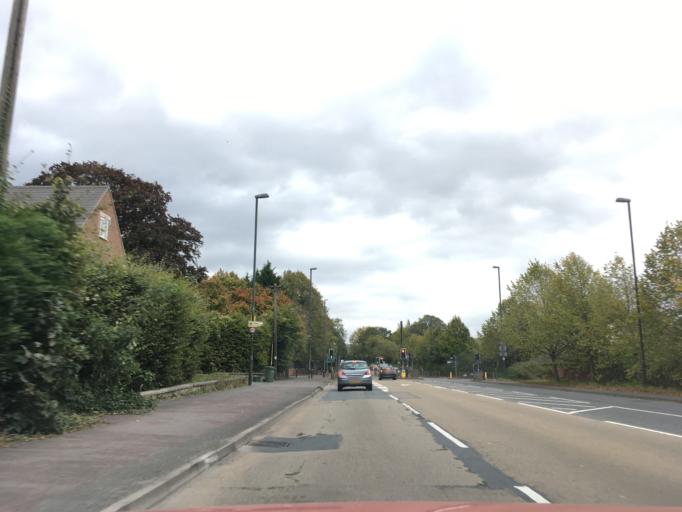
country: GB
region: England
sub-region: Gloucestershire
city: Stonehouse
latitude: 51.7427
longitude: -2.2851
